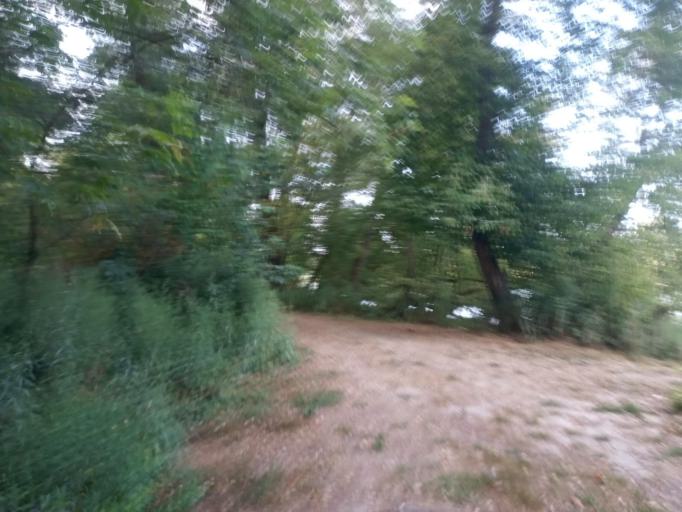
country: HU
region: Pest
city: Szentendre
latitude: 47.6380
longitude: 19.0831
